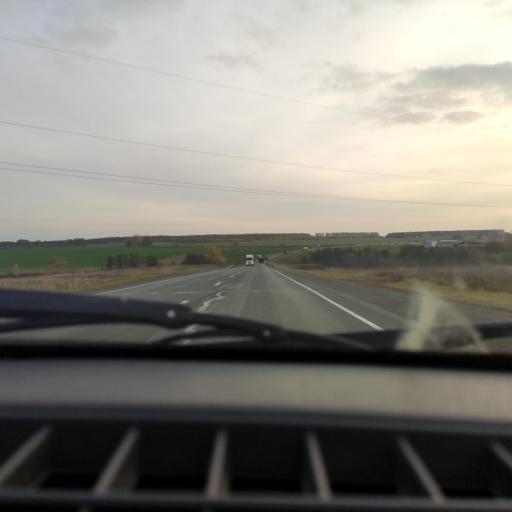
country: RU
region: Bashkortostan
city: Avdon
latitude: 54.7046
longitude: 55.7711
